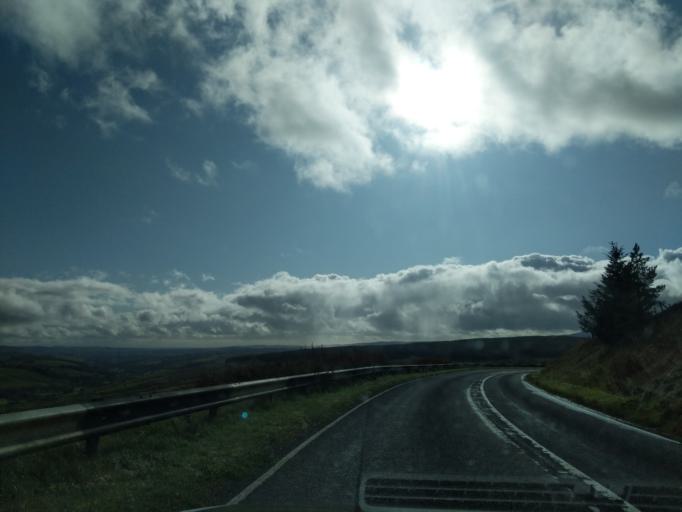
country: GB
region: Scotland
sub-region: Dumfries and Galloway
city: Moffat
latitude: 55.3945
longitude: -3.4800
